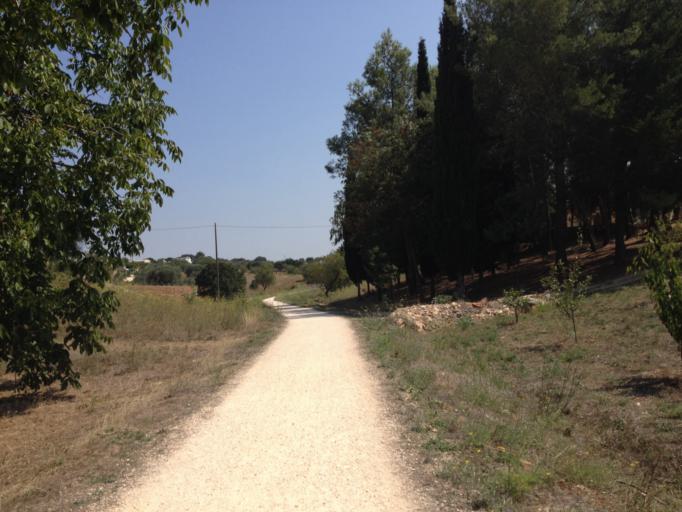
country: IT
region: Apulia
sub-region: Provincia di Brindisi
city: Cisternino
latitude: 40.7183
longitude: 17.4031
